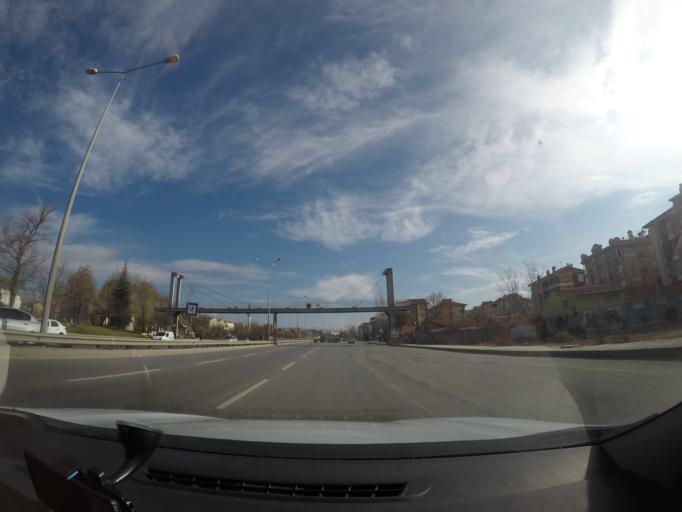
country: TR
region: Eskisehir
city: Eskisehir
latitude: 39.7919
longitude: 30.5096
